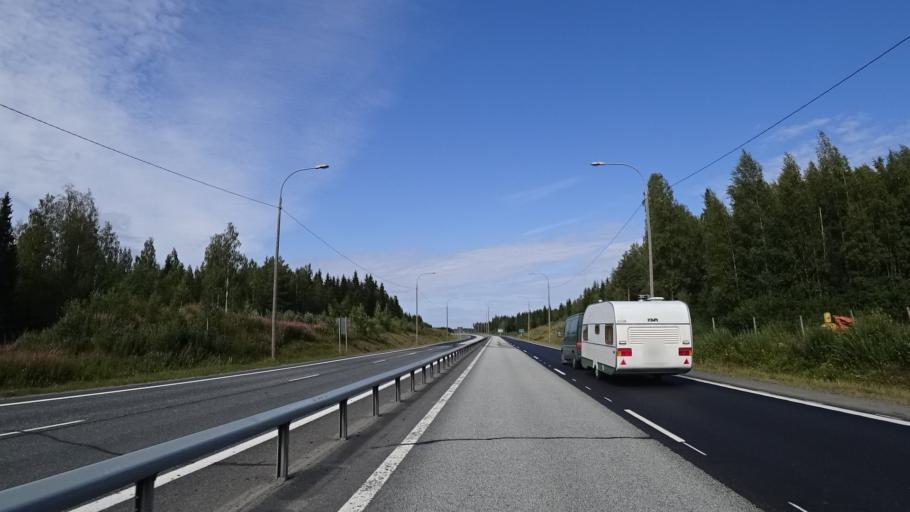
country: FI
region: North Karelia
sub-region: Joensuu
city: Joensuu
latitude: 62.5537
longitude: 29.8396
